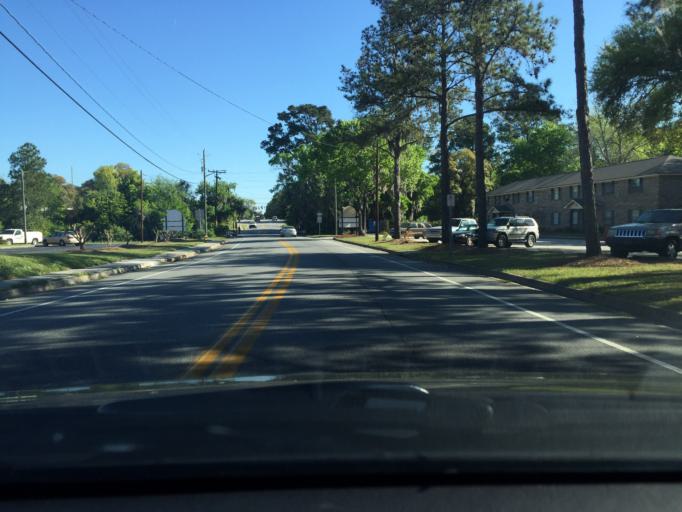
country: US
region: Georgia
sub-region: Chatham County
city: Montgomery
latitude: 31.9940
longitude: -81.1161
